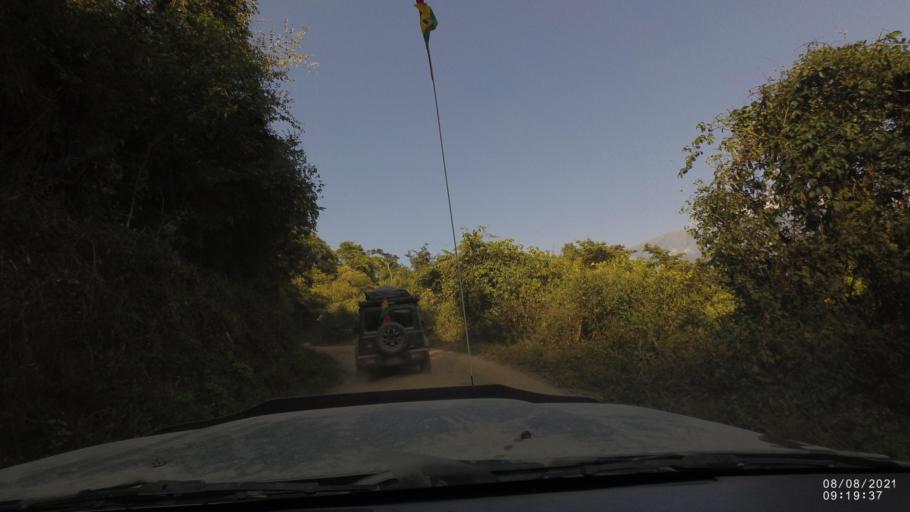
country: BO
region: La Paz
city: Quime
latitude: -16.5714
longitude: -66.7170
